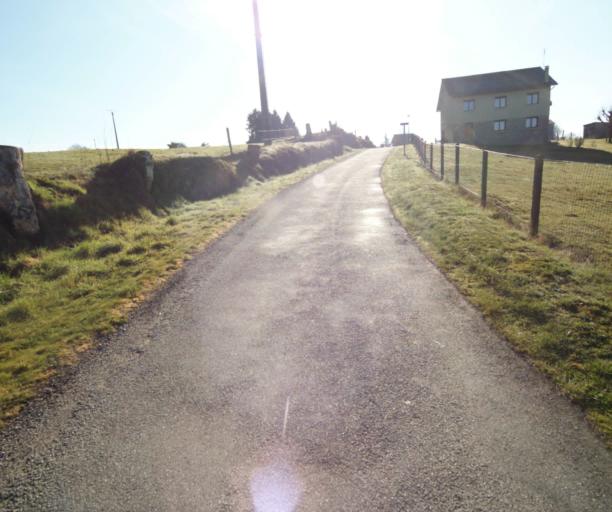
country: FR
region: Limousin
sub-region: Departement de la Correze
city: Correze
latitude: 45.3162
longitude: 1.8859
